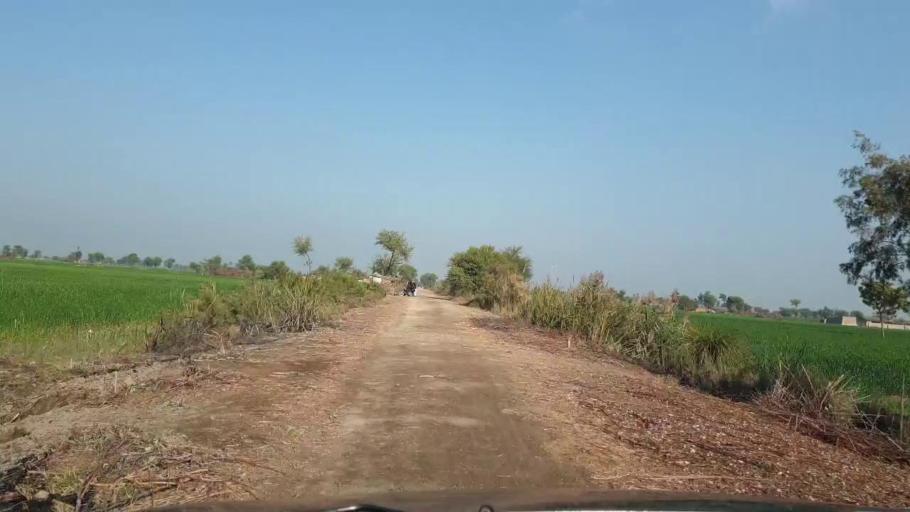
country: PK
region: Sindh
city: Sinjhoro
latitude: 26.0597
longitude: 68.7727
